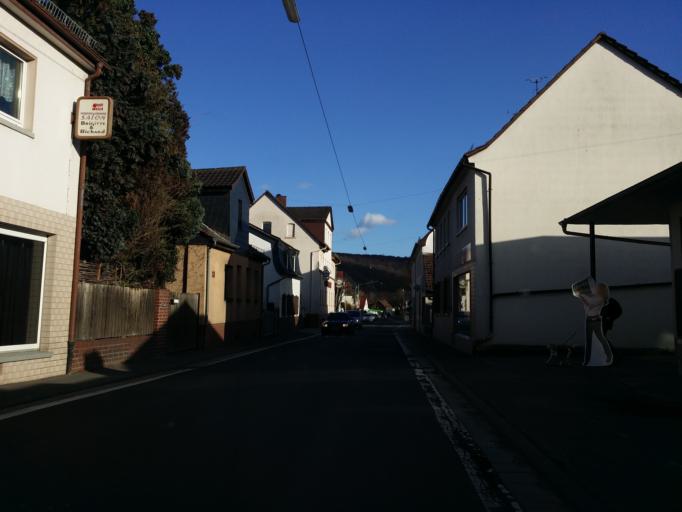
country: DE
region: Hesse
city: Kelkheim (Taunus)
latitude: 50.1165
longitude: 8.4221
